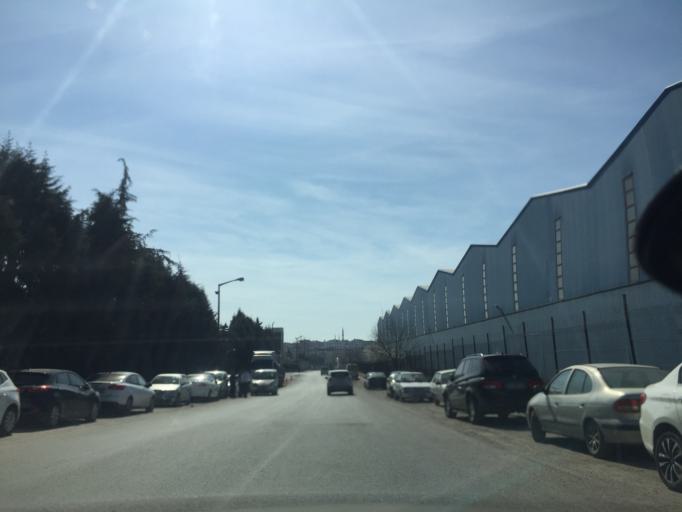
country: TR
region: Istanbul
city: Icmeler
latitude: 40.8389
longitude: 29.3167
